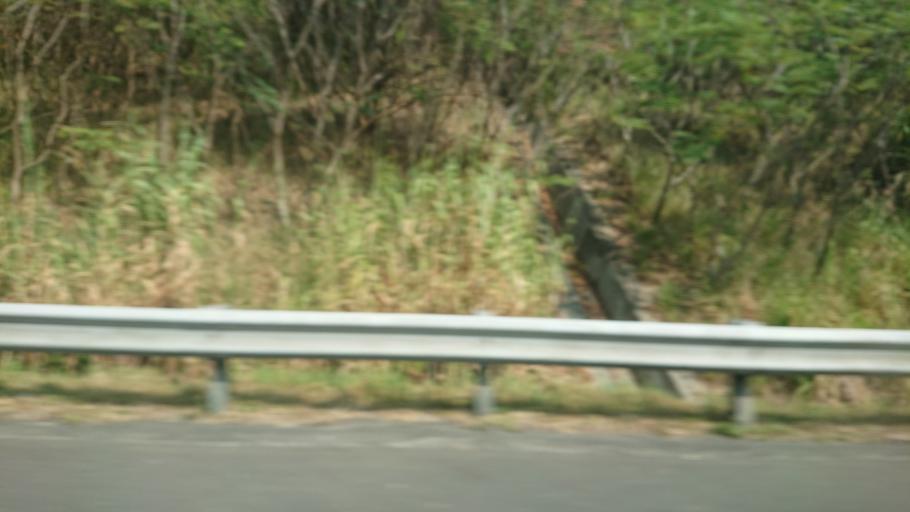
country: TW
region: Taiwan
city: Lugu
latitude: 23.7783
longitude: 120.6826
